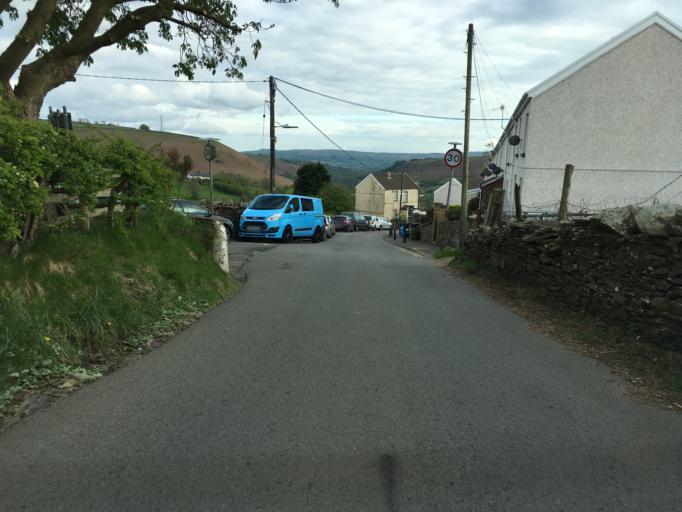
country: GB
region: Wales
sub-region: Merthyr Tydfil County Borough
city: Treharris
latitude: 51.7068
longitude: -3.3107
